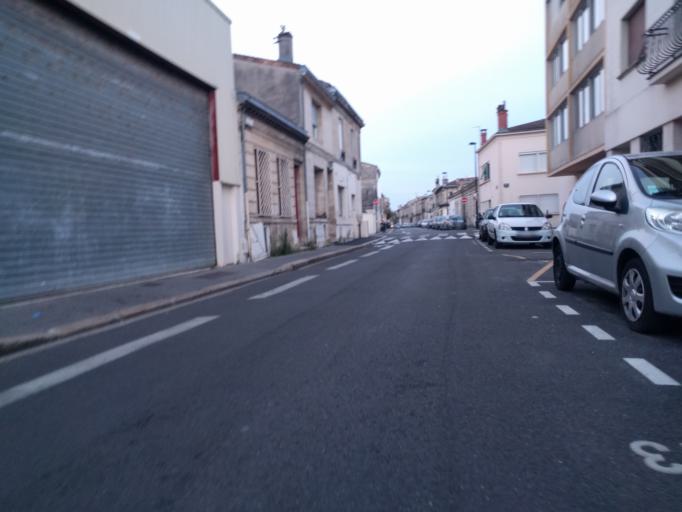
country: FR
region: Aquitaine
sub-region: Departement de la Gironde
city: Bordeaux
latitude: 44.8210
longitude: -0.5780
